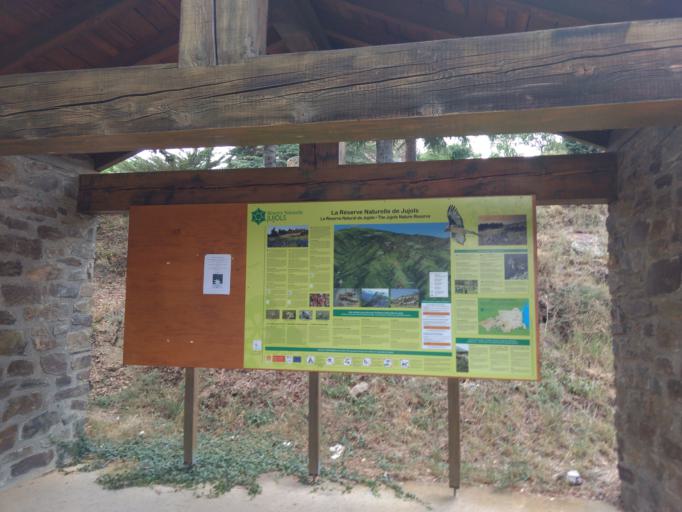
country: FR
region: Languedoc-Roussillon
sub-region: Departement des Pyrenees-Orientales
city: Vernet-les-Bains
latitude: 42.5695
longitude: 2.2948
